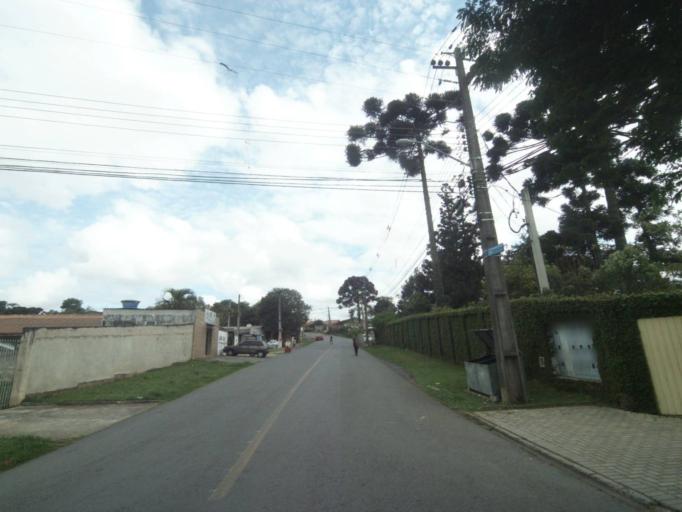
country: BR
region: Parana
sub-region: Curitiba
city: Curitiba
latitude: -25.3785
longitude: -49.2926
